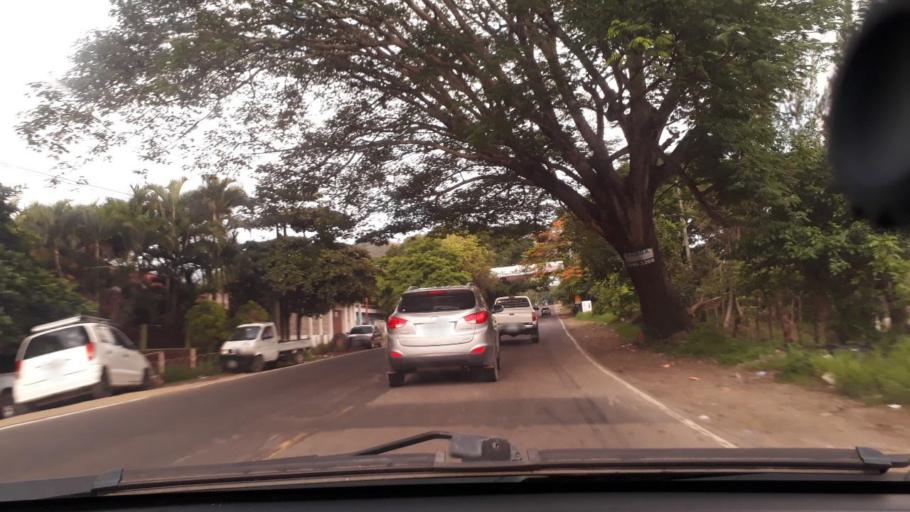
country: GT
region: Jutiapa
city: Quesada
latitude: 14.2751
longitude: -90.0024
